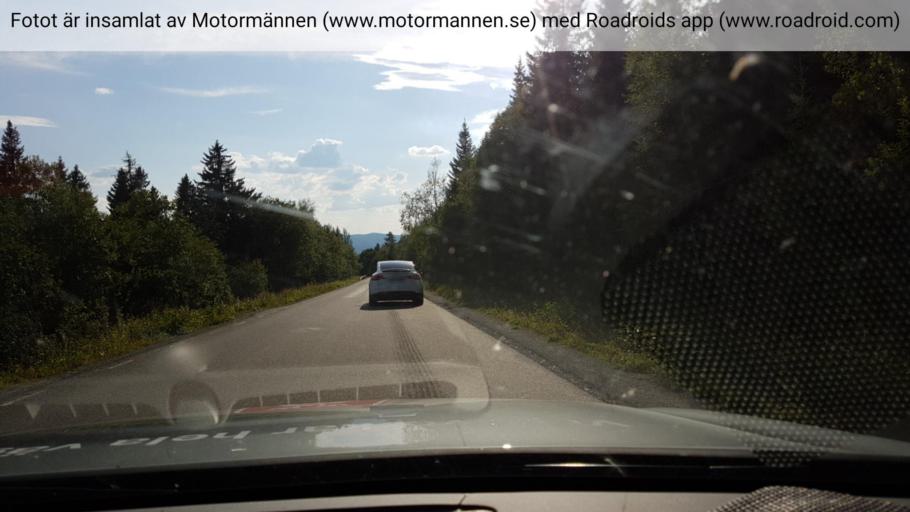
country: SE
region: Jaemtland
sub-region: Are Kommun
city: Are
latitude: 63.4095
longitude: 13.0361
